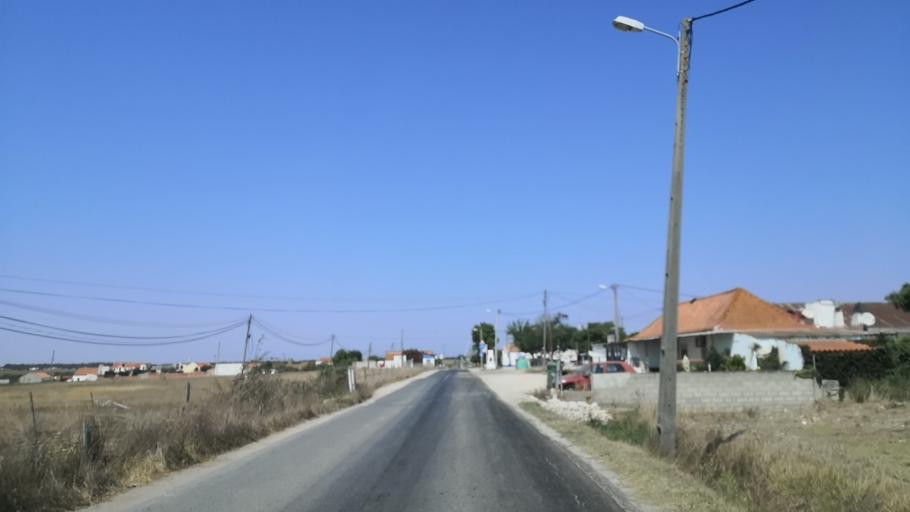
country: PT
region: Santarem
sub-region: Benavente
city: Poceirao
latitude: 38.6990
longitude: -8.7246
